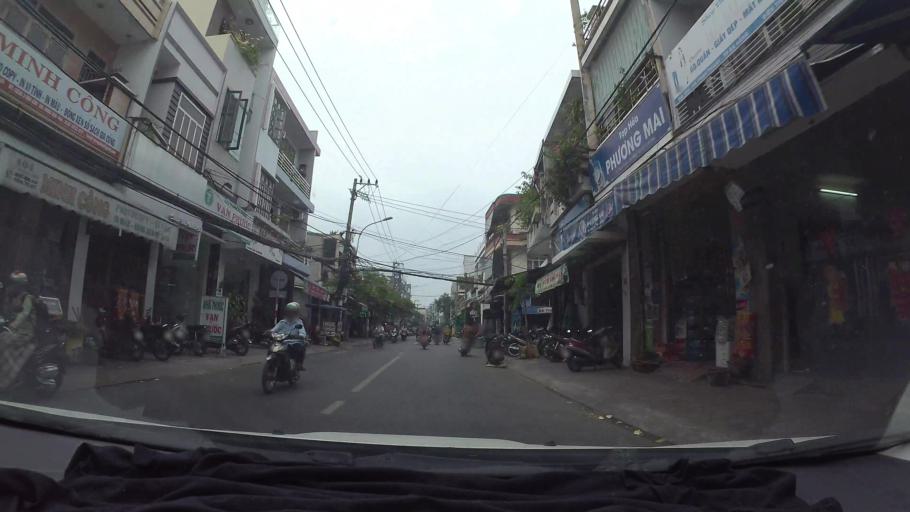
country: VN
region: Da Nang
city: Da Nang
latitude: 16.0623
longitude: 108.2090
